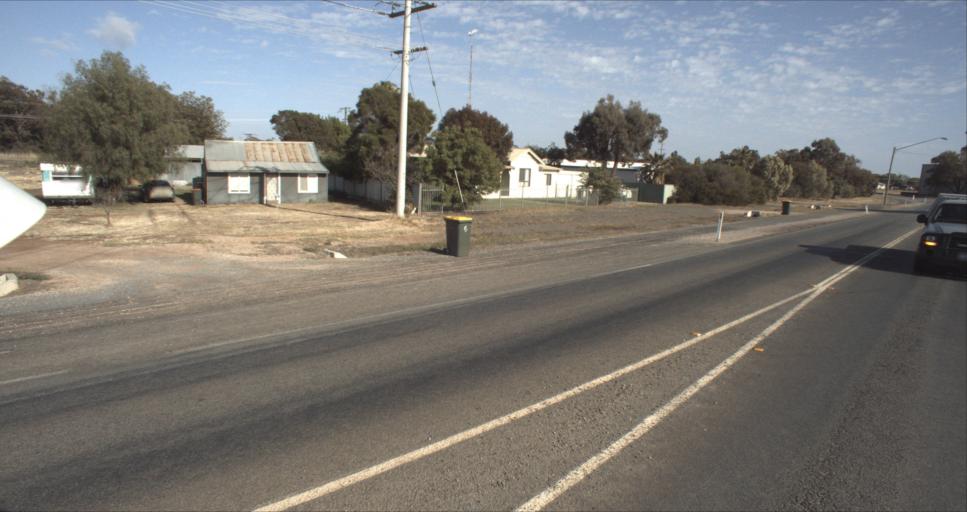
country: AU
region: New South Wales
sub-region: Leeton
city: Leeton
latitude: -34.5617
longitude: 146.3926
